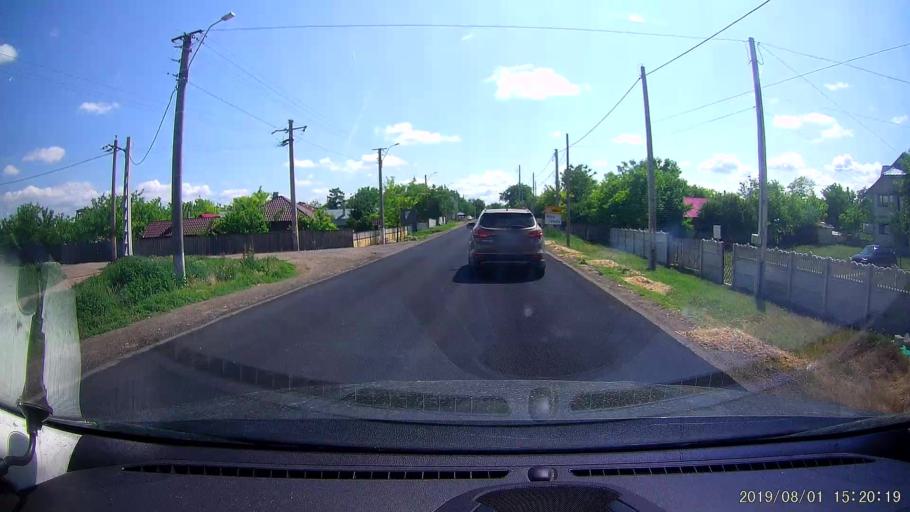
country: RO
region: Braila
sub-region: Comuna Tufesti
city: Tufesti
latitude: 45.0802
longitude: 27.8076
